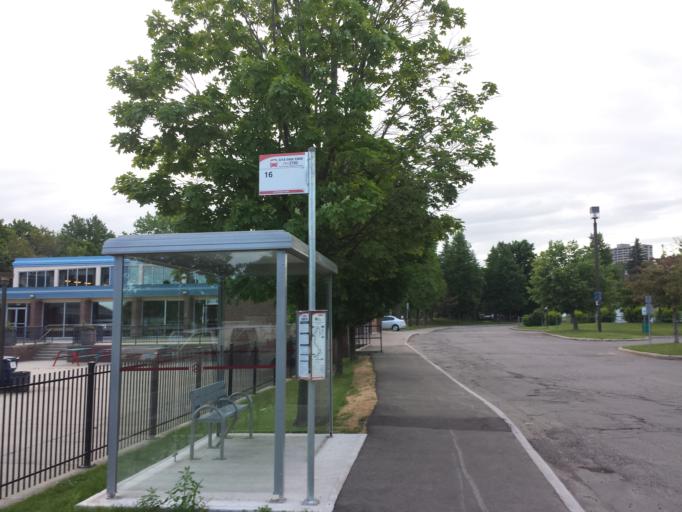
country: CA
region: Ontario
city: Bells Corners
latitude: 45.3638
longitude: -75.8023
